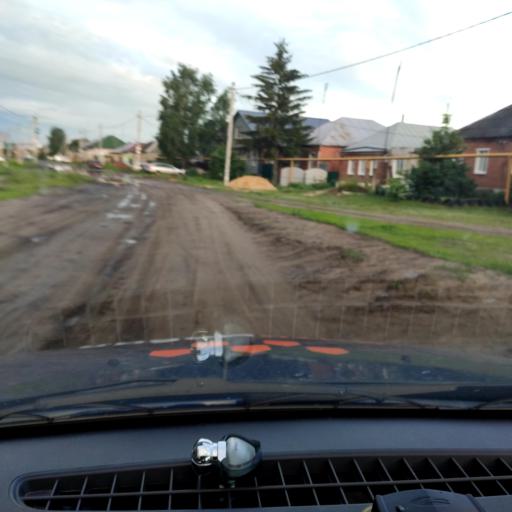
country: RU
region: Voronezj
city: Somovo
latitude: 51.7528
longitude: 39.3253
